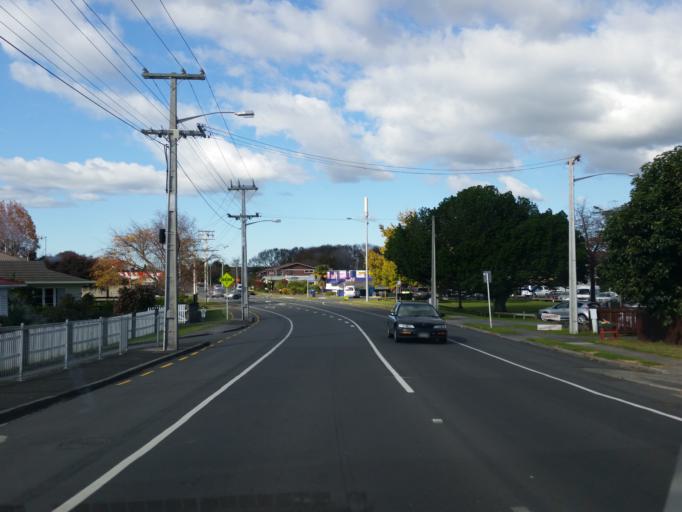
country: NZ
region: Bay of Plenty
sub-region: Tauranga City
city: Tauranga
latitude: -37.6673
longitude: 176.1525
